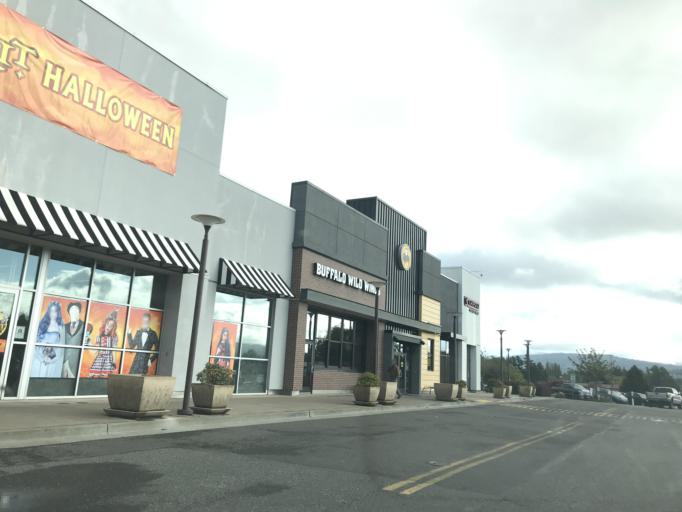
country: US
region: Washington
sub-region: Whatcom County
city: Bellingham
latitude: 48.7848
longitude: -122.4903
